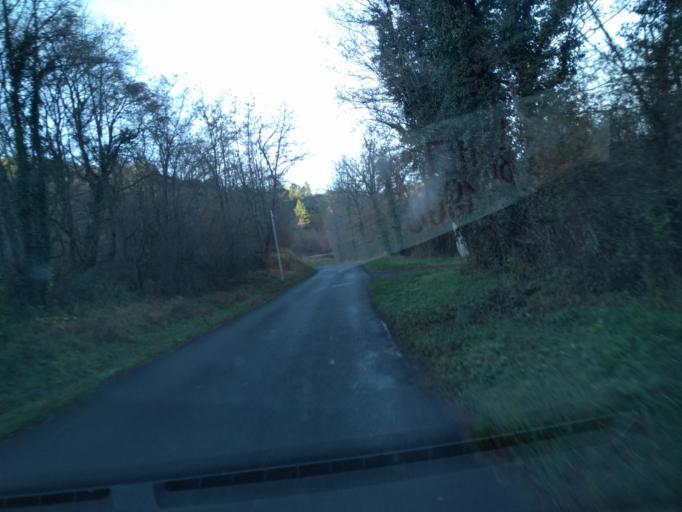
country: FR
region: Languedoc-Roussillon
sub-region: Departement de l'Aude
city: Quillan
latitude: 42.8962
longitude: 2.1873
